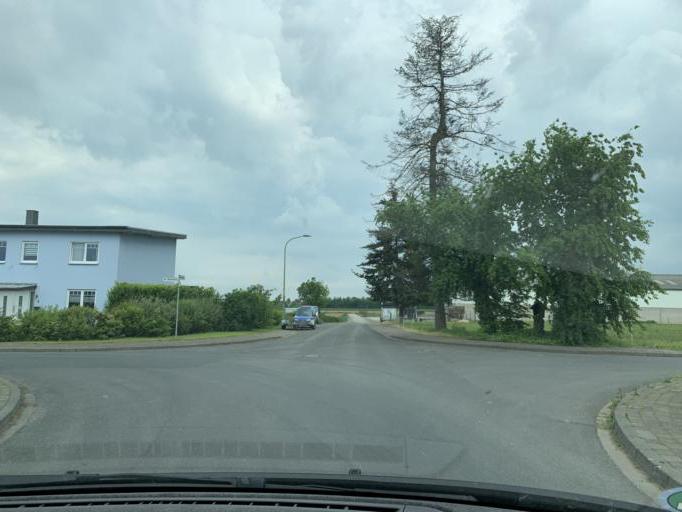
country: DE
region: North Rhine-Westphalia
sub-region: Regierungsbezirk Koln
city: Vettweiss
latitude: 50.7433
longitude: 6.6067
